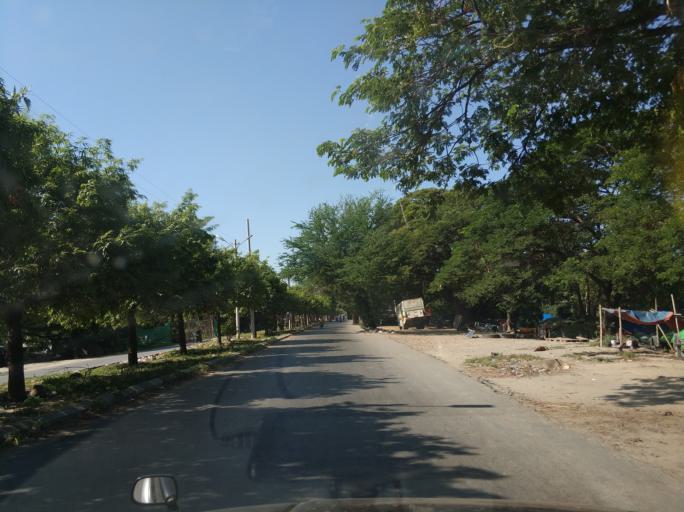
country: MM
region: Mandalay
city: Mandalay
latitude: 21.9649
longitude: 96.0560
